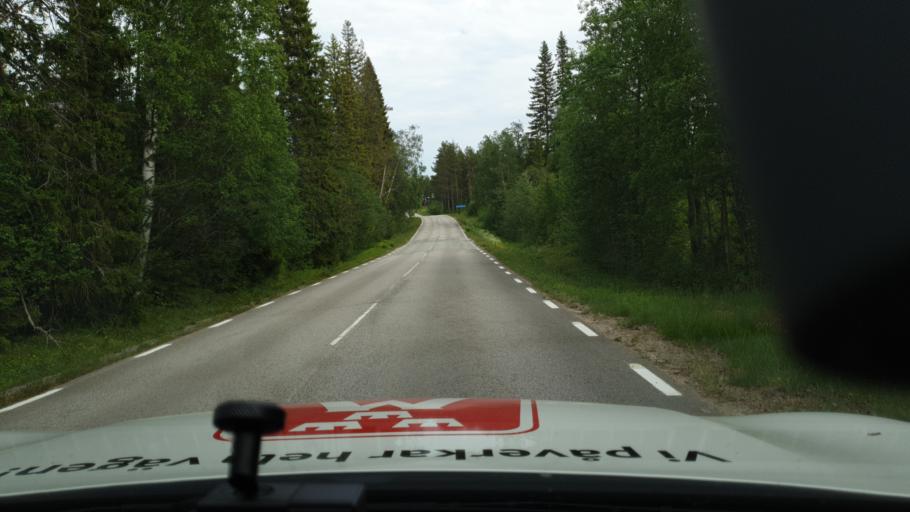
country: SE
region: Vaesterbotten
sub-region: Umea Kommun
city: Hoernefors
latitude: 63.5632
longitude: 19.7643
